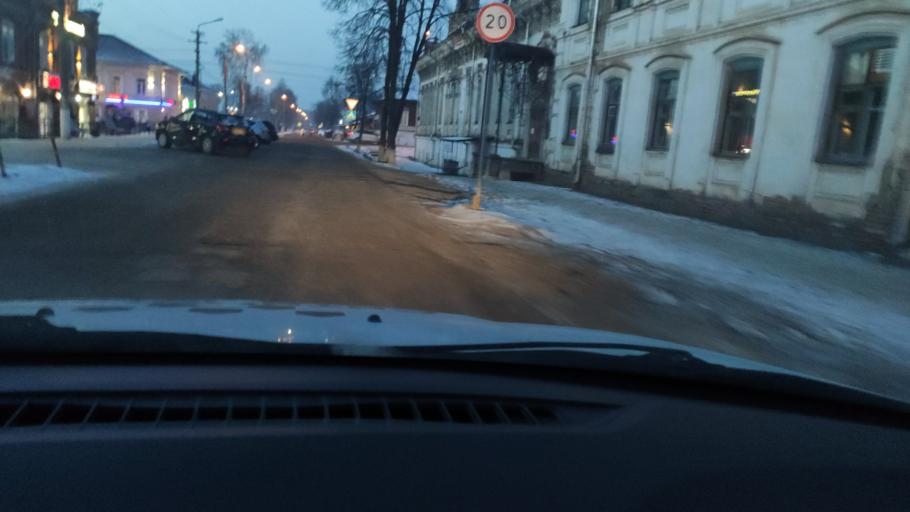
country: RU
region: Perm
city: Kungur
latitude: 57.4371
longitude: 56.9368
